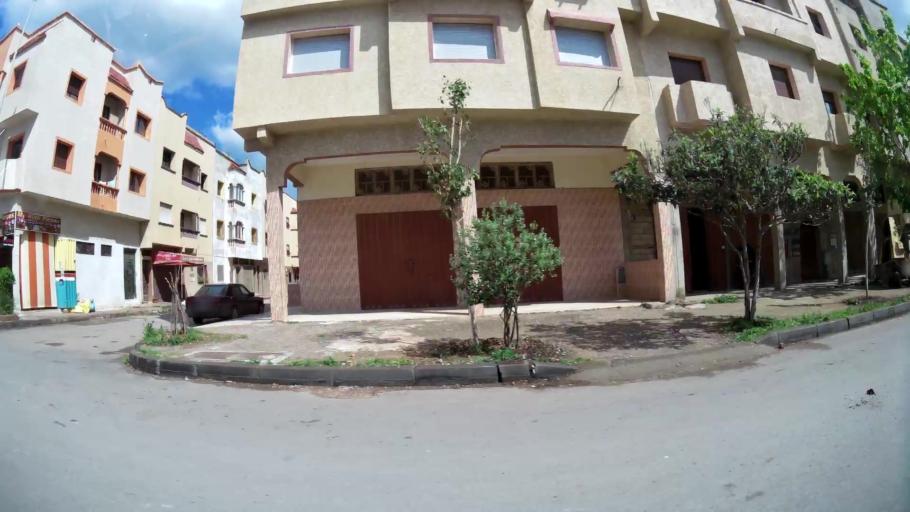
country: MA
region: Grand Casablanca
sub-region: Mediouna
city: Mediouna
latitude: 33.3769
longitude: -7.5362
